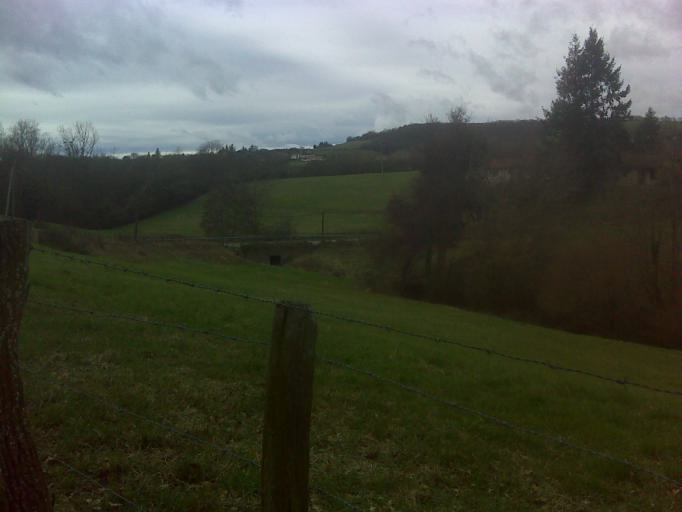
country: FR
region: Rhone-Alpes
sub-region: Departement du Rhone
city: Lentilly
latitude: 45.8139
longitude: 4.6531
